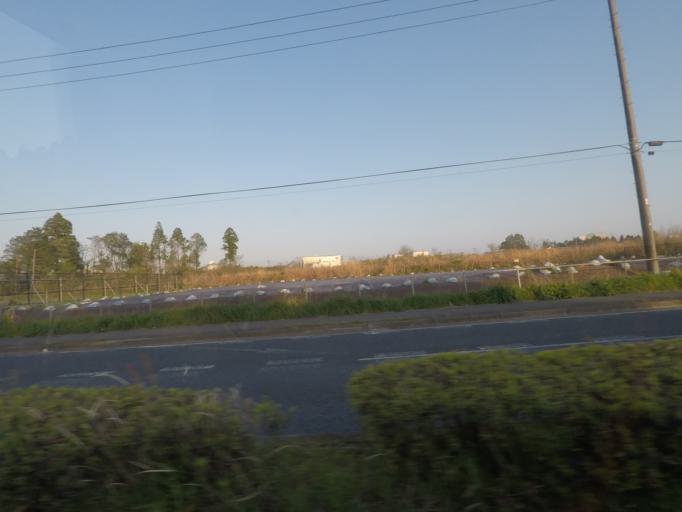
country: JP
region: Chiba
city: Narita
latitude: 35.7661
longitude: 140.3096
